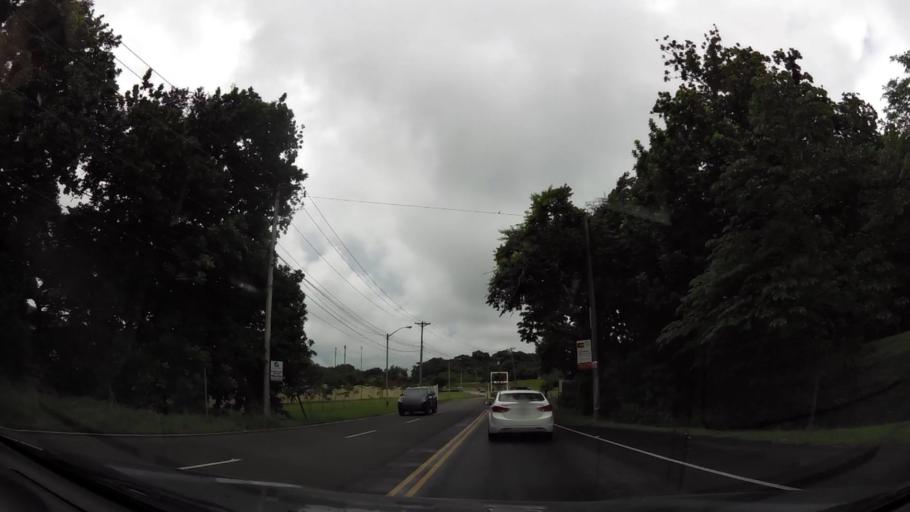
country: PA
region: Panama
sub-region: Distrito de Panama
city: Ancon
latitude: 8.9921
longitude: -79.5539
